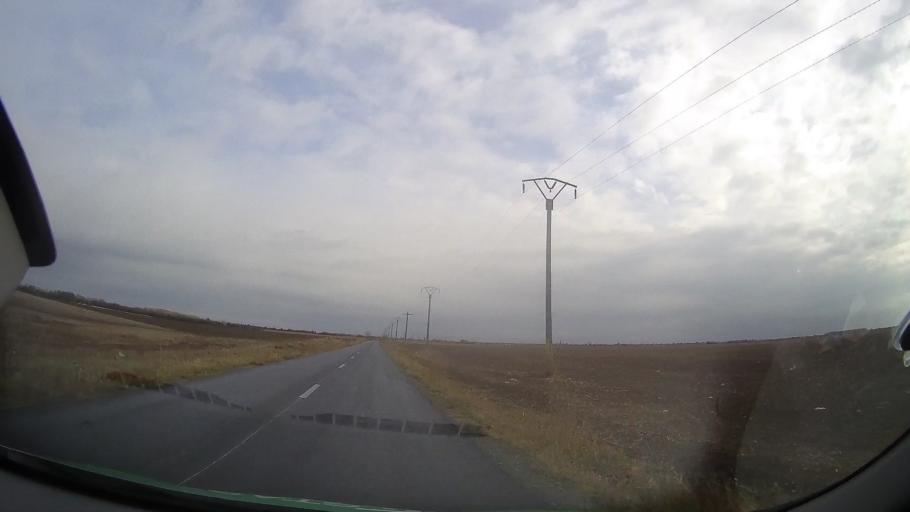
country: RO
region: Ialomita
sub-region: Comuna Maia
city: Maia
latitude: 44.7560
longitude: 26.3788
